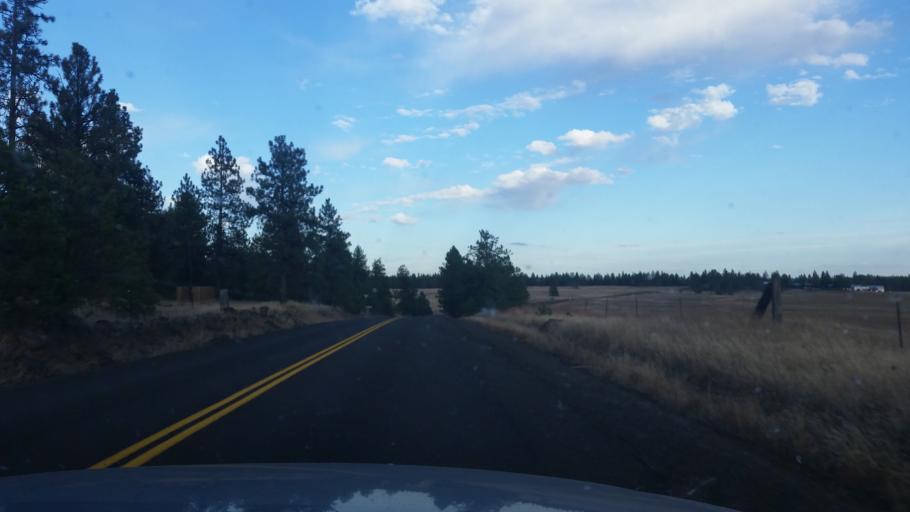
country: US
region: Washington
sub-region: Spokane County
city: Medical Lake
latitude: 47.4533
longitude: -117.8080
